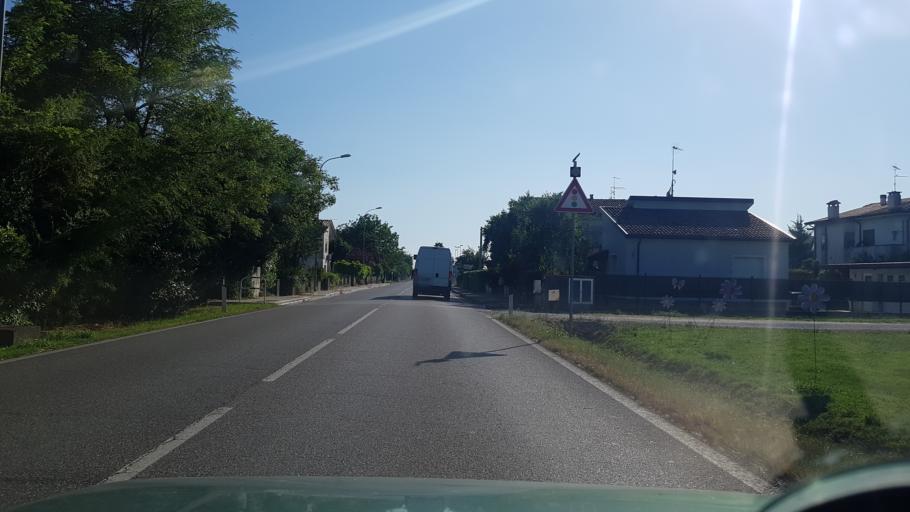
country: IT
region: Friuli Venezia Giulia
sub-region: Provincia di Udine
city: Ruda
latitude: 45.8428
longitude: 13.4001
